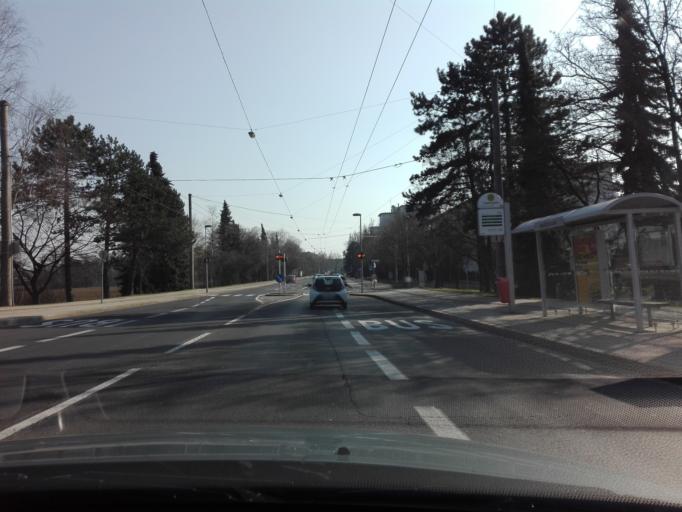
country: AT
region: Upper Austria
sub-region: Politischer Bezirk Linz-Land
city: Leonding
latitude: 48.2625
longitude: 14.2899
